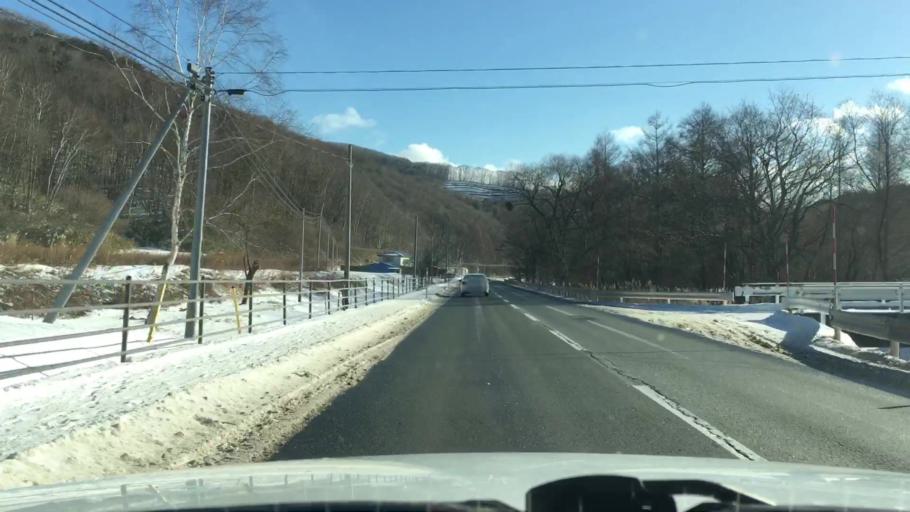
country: JP
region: Iwate
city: Morioka-shi
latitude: 39.6415
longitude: 141.4167
